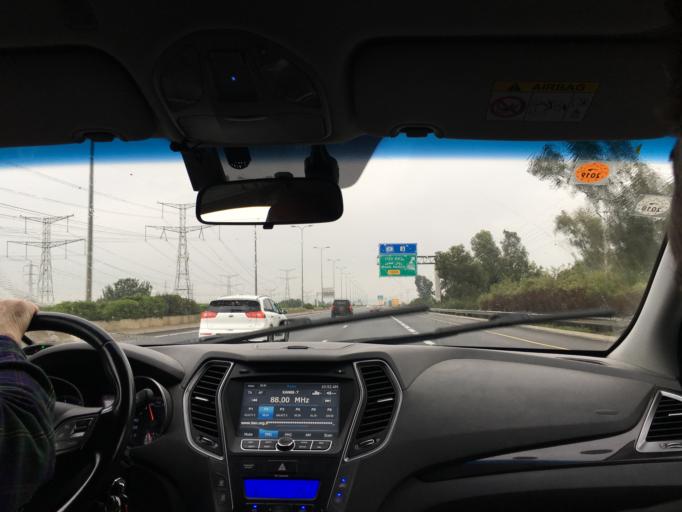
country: IL
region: Central District
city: Petah Tiqwa
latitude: 32.1196
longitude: 34.9136
